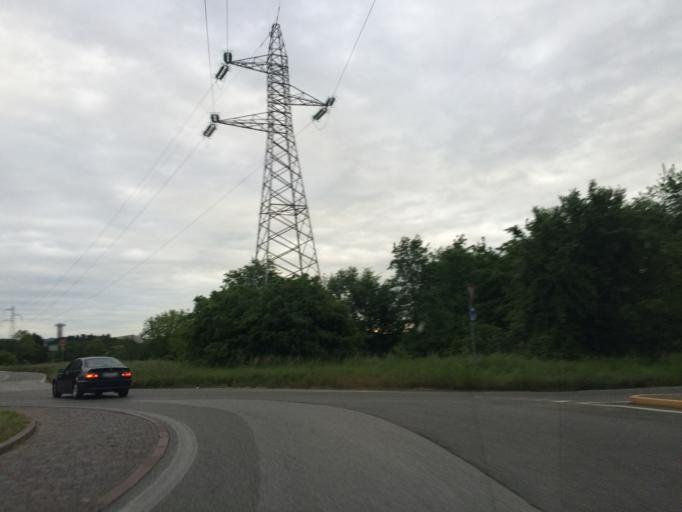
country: IT
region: Lombardy
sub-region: Provincia di Brescia
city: San Zeno Naviglio
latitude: 45.5103
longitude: 10.2378
